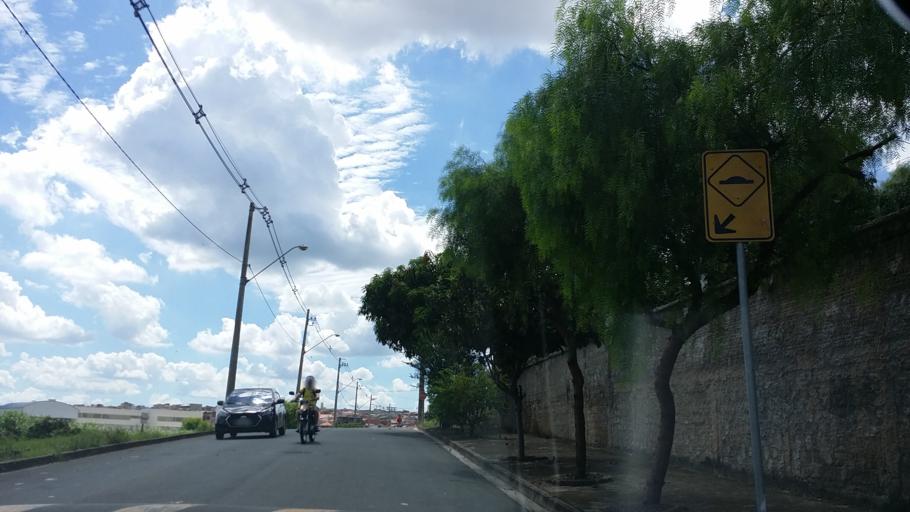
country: BR
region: Sao Paulo
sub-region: Indaiatuba
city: Indaiatuba
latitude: -23.1307
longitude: -47.2458
